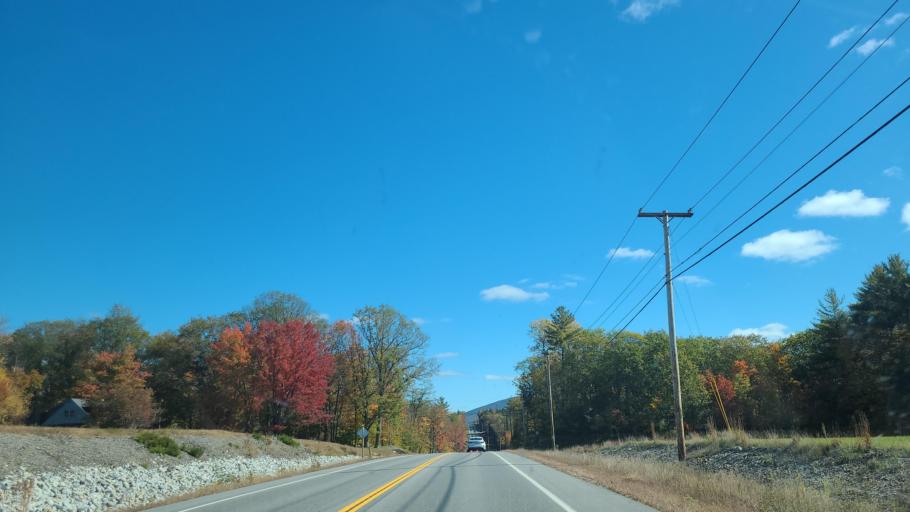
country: US
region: Maine
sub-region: Oxford County
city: Fryeburg
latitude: 44.0240
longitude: -70.9424
